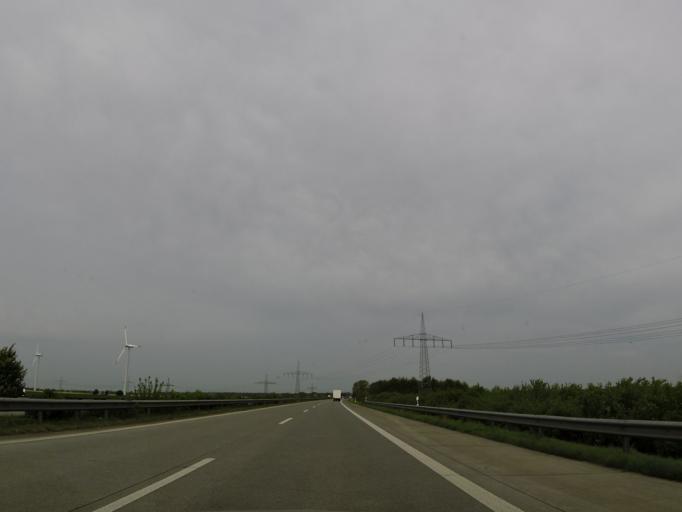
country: DE
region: Schleswig-Holstein
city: Rethwisch
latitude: 53.8516
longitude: 9.5846
